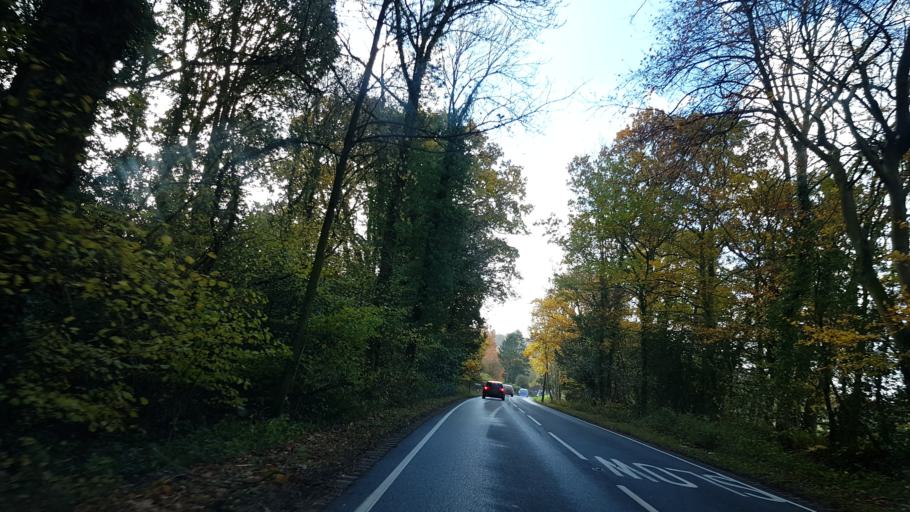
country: GB
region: England
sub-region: Surrey
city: Haslemere
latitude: 51.1097
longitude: -0.6865
